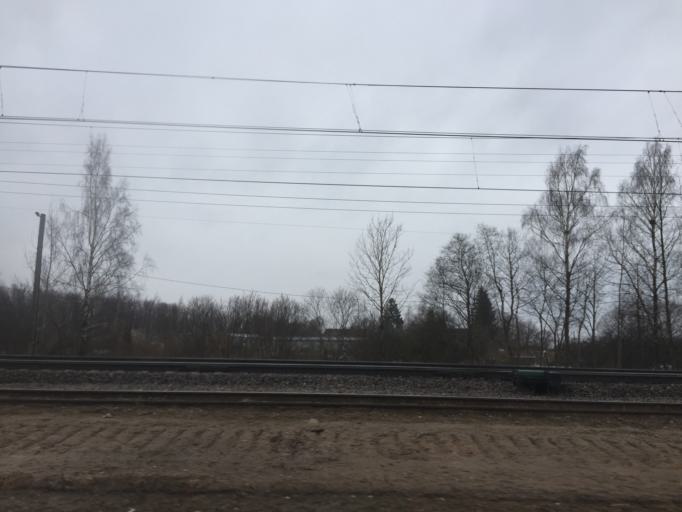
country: LV
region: Lielvarde
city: Lielvarde
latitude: 56.7233
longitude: 24.8005
